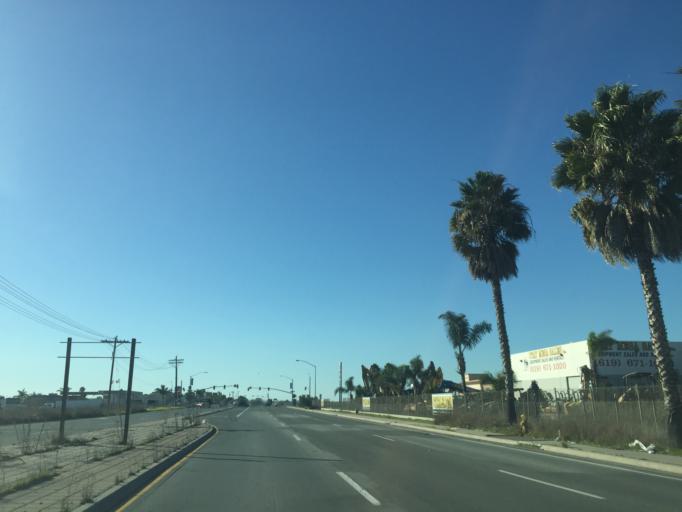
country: MX
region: Baja California
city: Tijuana
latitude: 32.5678
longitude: -116.9598
